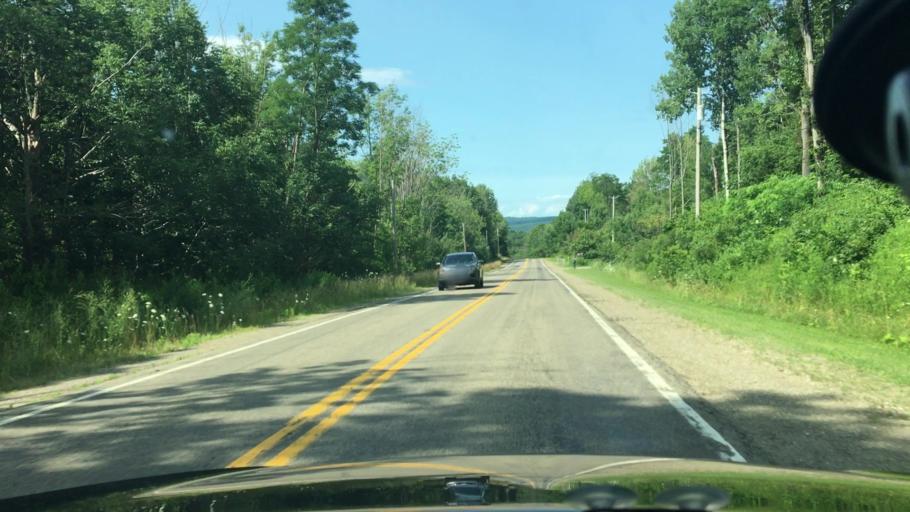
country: US
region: New York
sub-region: Chautauqua County
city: Lakewood
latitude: 42.2457
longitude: -79.3575
